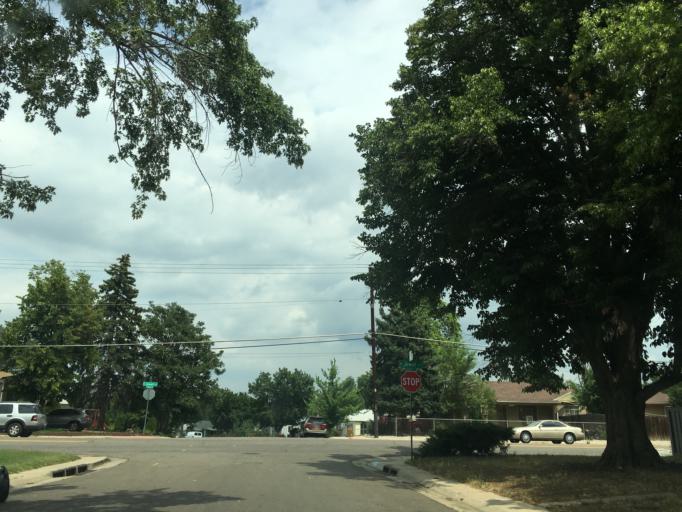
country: US
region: Colorado
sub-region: Arapahoe County
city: Sheridan
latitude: 39.6818
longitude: -105.0321
